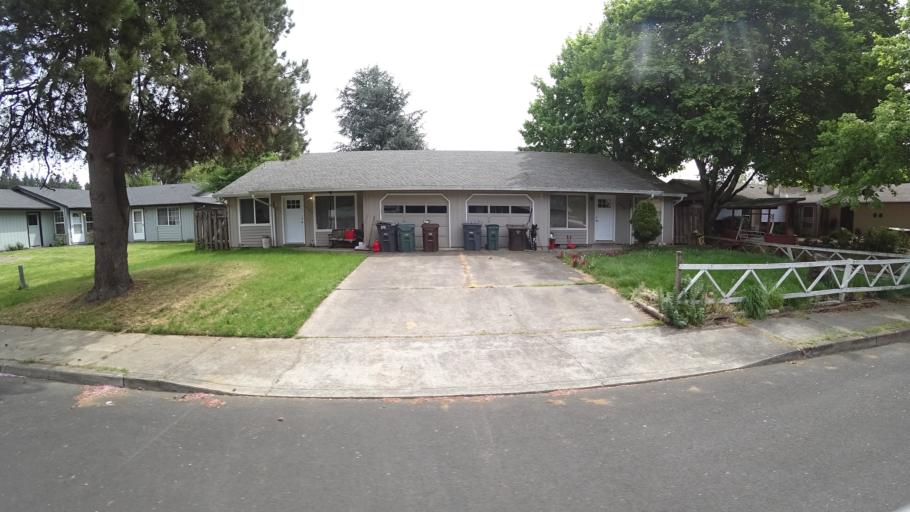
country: US
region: Oregon
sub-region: Washington County
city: Hillsboro
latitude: 45.5324
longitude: -122.9917
